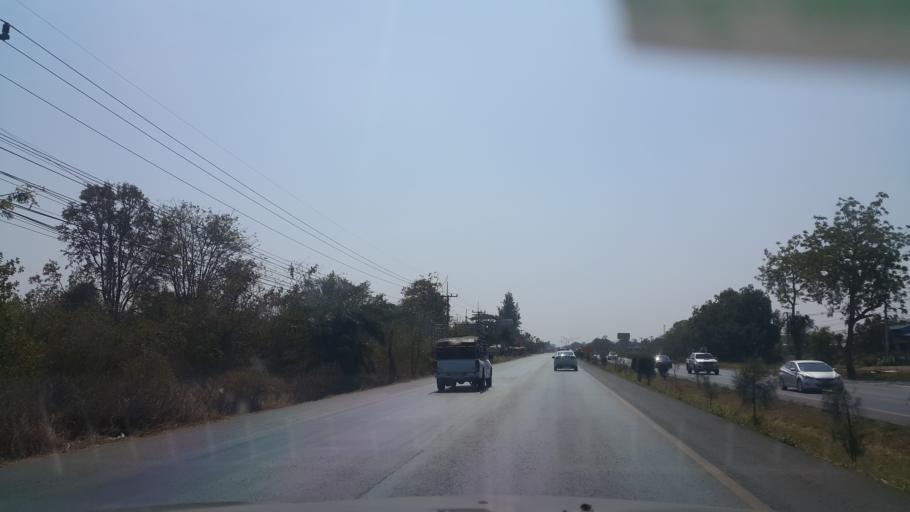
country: TH
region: Khon Kaen
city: Non Sila
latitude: 16.0100
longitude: 102.7048
